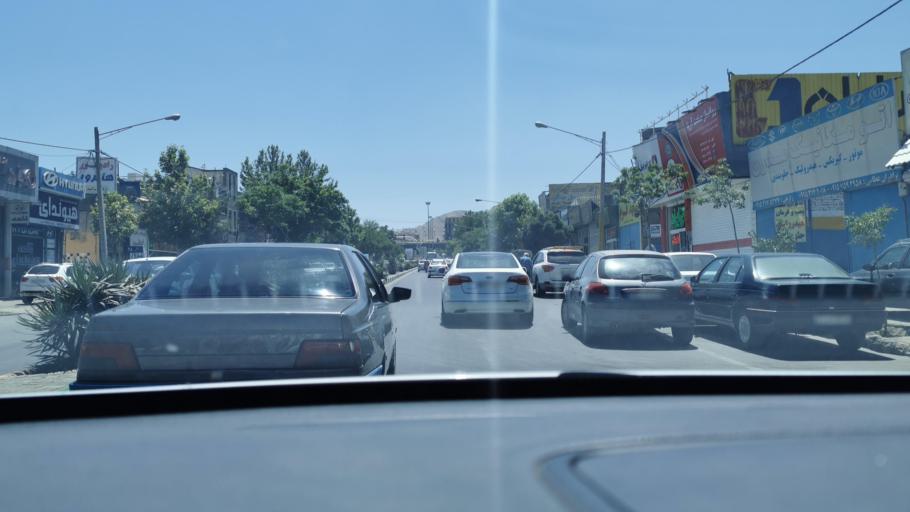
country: IR
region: Razavi Khorasan
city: Mashhad
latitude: 36.2590
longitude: 59.6014
